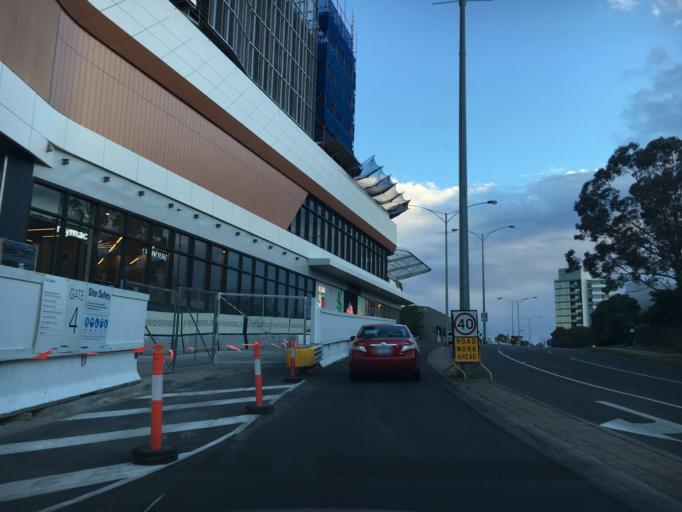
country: AU
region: Victoria
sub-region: Whitehorse
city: Vermont South
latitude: -37.8772
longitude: 145.1643
